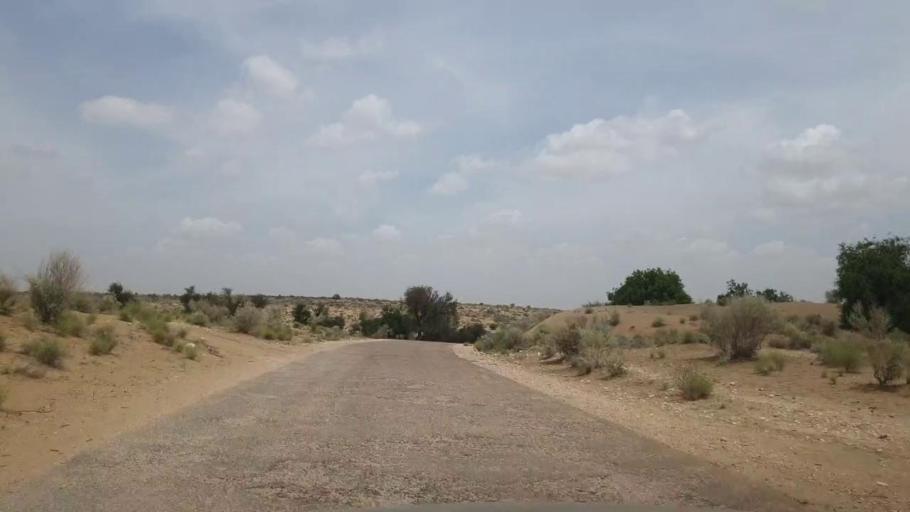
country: PK
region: Sindh
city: Kot Diji
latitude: 27.1813
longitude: 69.1829
